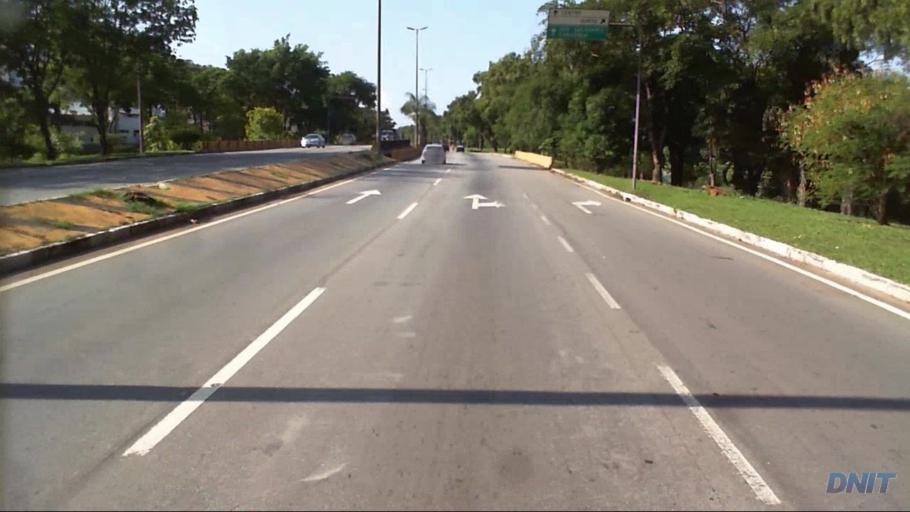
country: BR
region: Minas Gerais
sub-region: Ipatinga
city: Ipatinga
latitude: -19.5067
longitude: -42.5703
